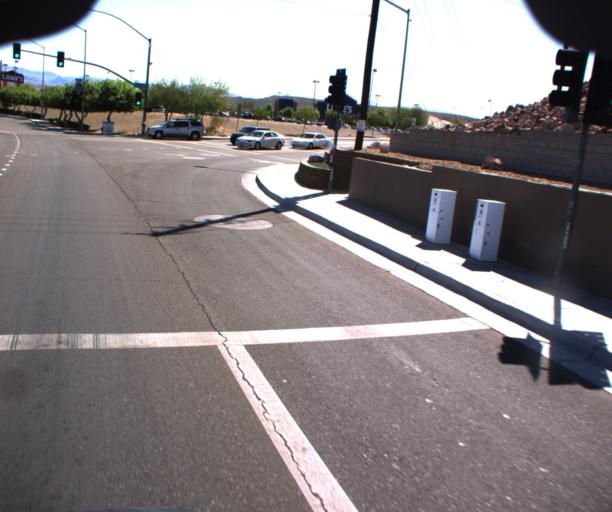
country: US
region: Arizona
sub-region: Mohave County
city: Bullhead City
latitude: 35.1226
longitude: -114.5825
